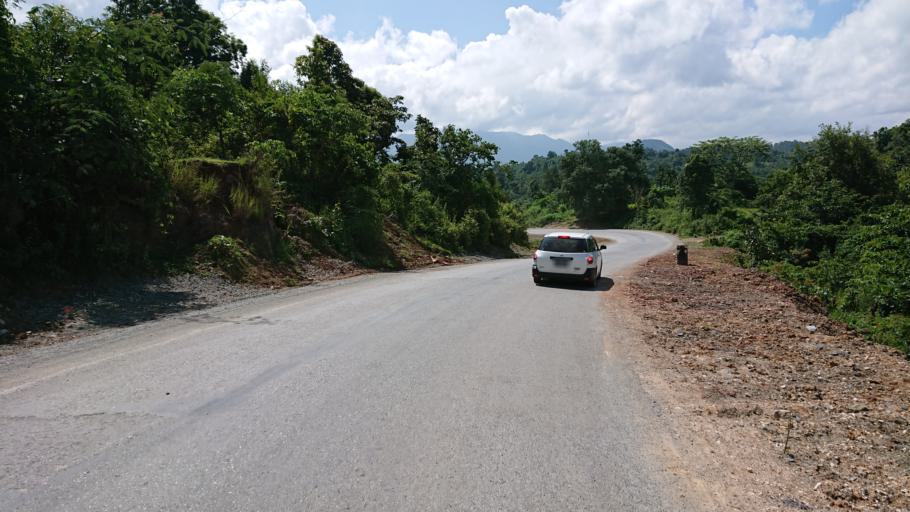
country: MM
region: Shan
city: Taunggyi
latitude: 20.8143
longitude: 97.3177
